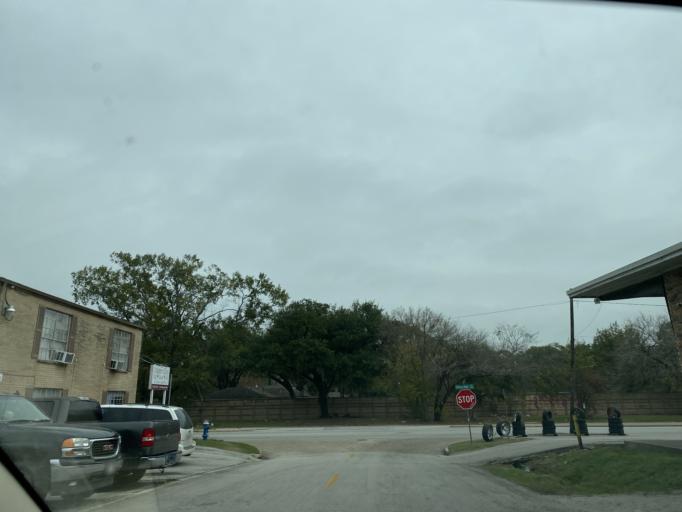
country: US
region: Texas
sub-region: Harris County
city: Bellaire
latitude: 29.7275
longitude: -95.4769
